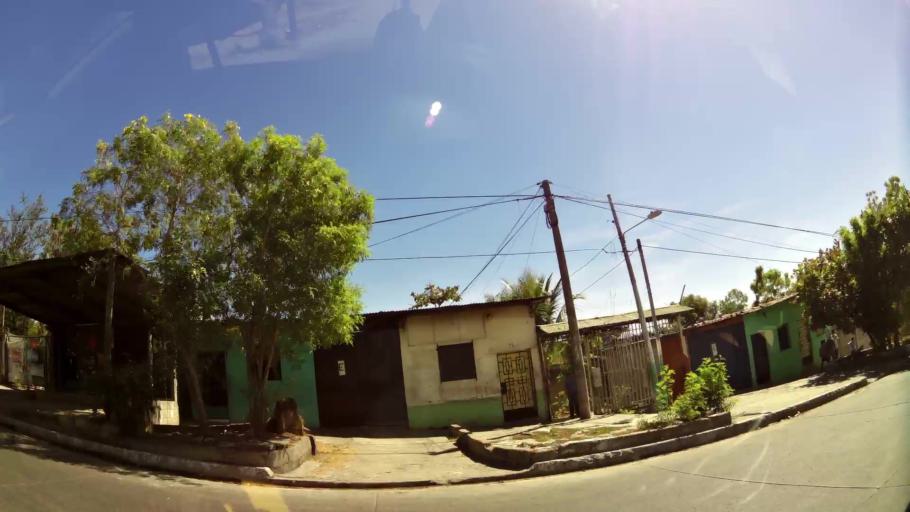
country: SV
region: San Salvador
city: Apopa
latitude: 13.8137
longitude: -89.1776
